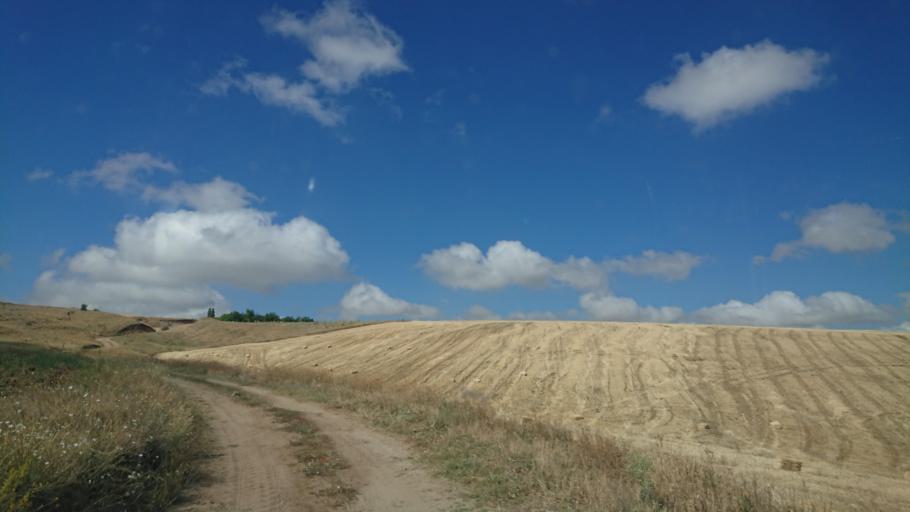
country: TR
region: Aksaray
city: Agacoren
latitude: 38.8490
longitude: 33.9388
